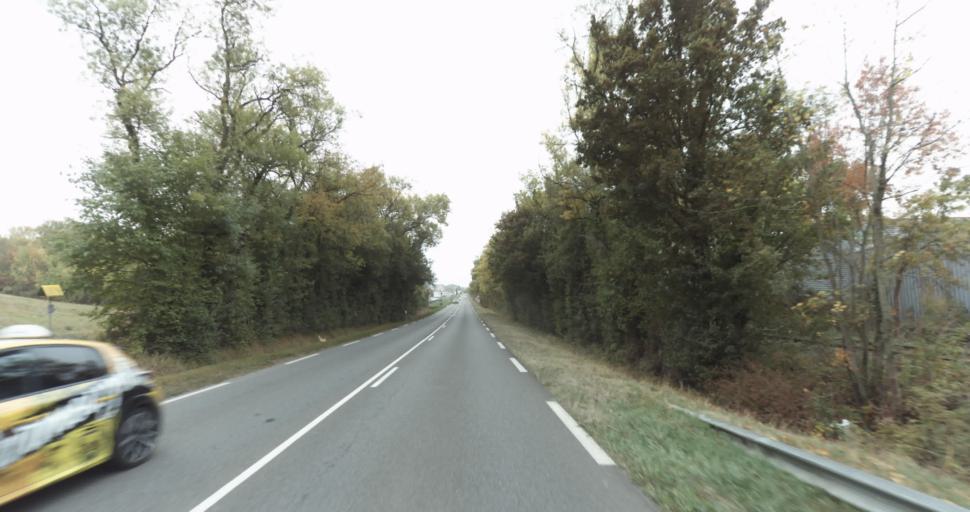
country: FR
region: Midi-Pyrenees
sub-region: Departement du Gers
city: Auch
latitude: 43.6734
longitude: 0.6017
